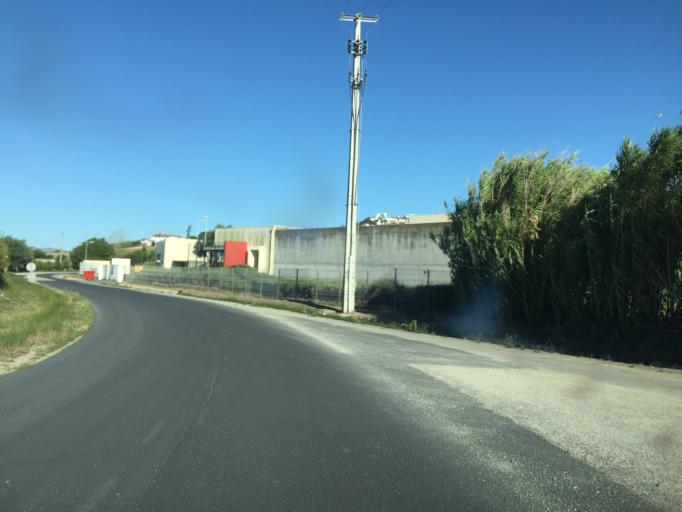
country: PT
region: Lisbon
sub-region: Torres Vedras
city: Torres Vedras
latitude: 39.0946
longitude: -9.2876
